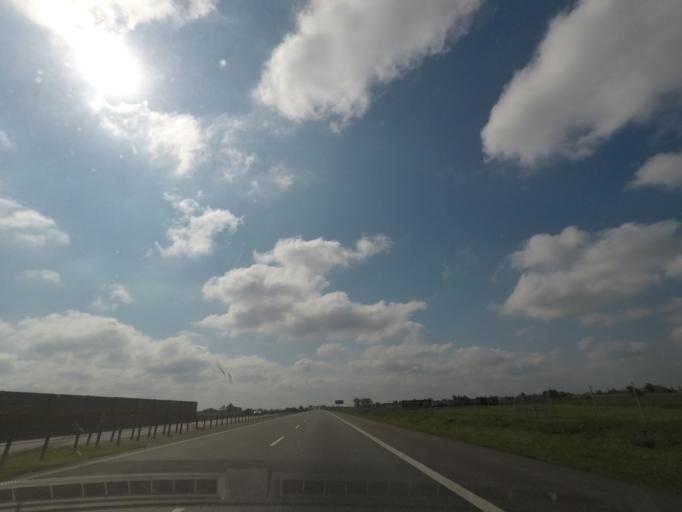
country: PL
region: Kujawsko-Pomorskie
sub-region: Powiat torunski
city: Lubicz Dolny
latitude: 53.1188
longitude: 18.7418
